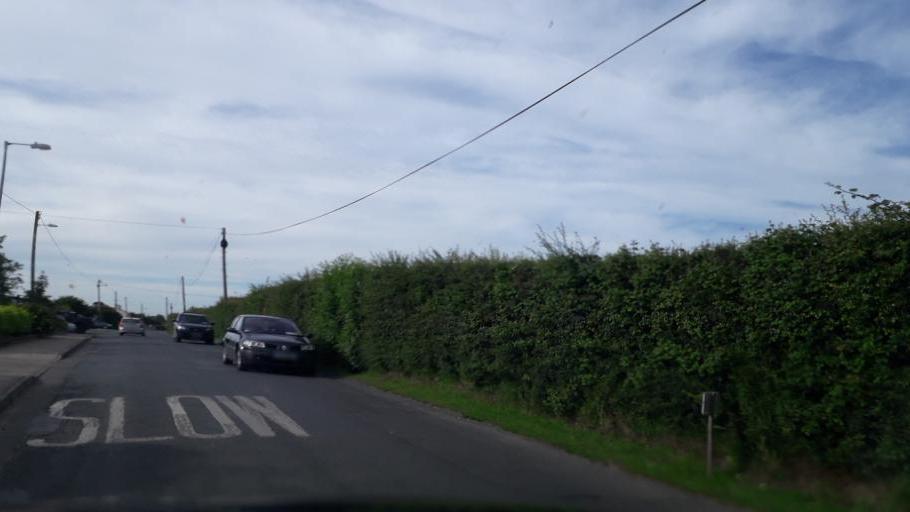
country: IE
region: Leinster
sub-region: Loch Garman
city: Courtown
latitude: 52.5756
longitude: -6.2298
